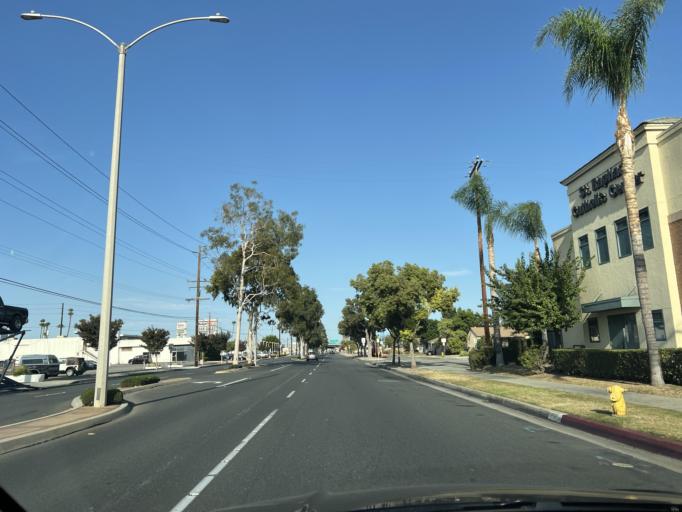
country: US
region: California
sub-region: Los Angeles County
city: Norwalk
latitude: 33.9023
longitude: -118.0691
